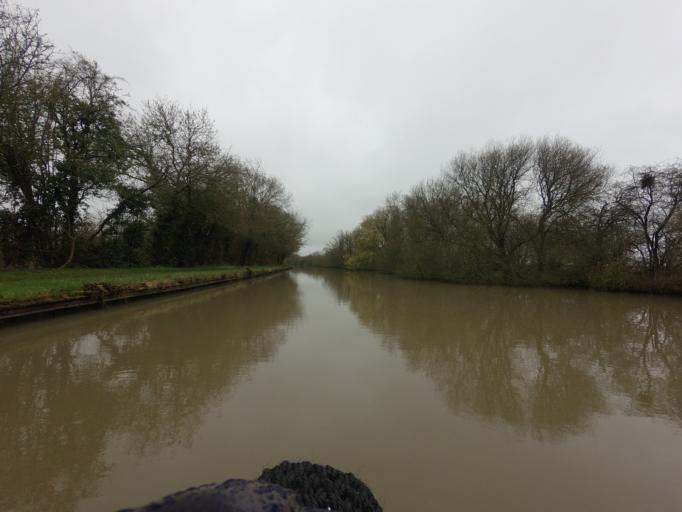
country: GB
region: England
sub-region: Milton Keynes
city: Castlethorpe
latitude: 52.0881
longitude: -0.8601
